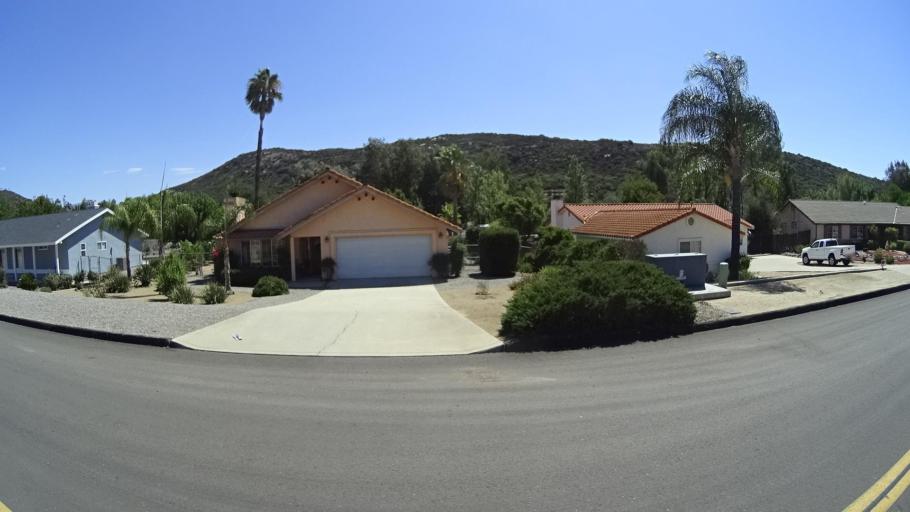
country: US
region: California
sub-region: San Diego County
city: San Diego Country Estates
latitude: 33.0110
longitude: -116.8110
